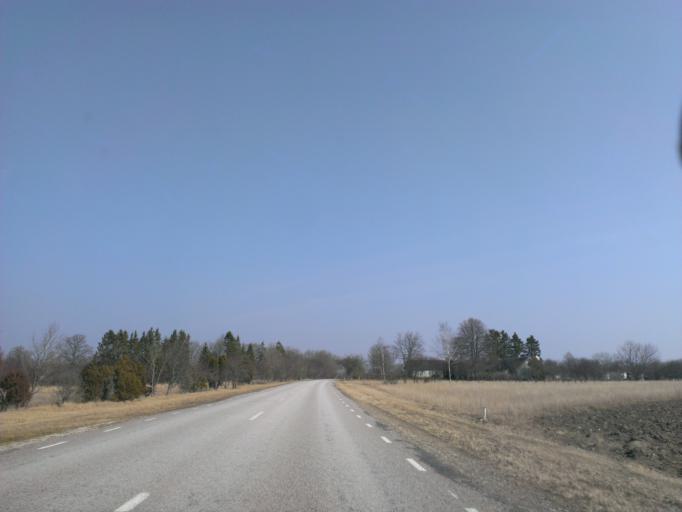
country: EE
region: Saare
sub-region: Kuressaare linn
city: Kuressaare
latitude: 58.2835
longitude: 22.6492
